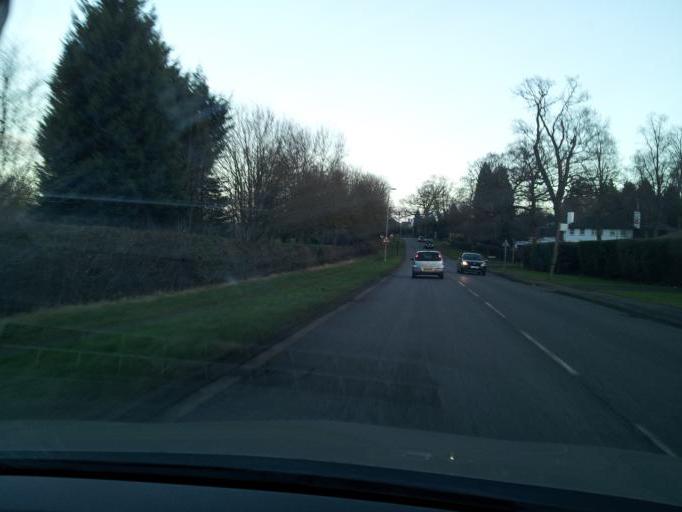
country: GB
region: England
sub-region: Leicestershire
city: Oadby
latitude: 52.6154
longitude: -1.0890
